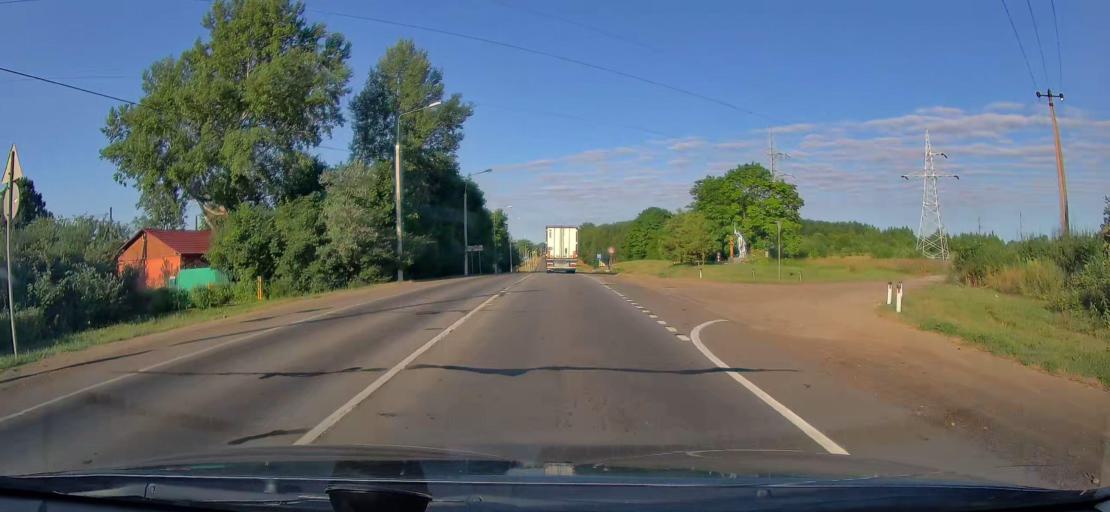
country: RU
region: Tula
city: Bol'shoye Skuratovo
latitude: 53.4534
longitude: 36.8628
